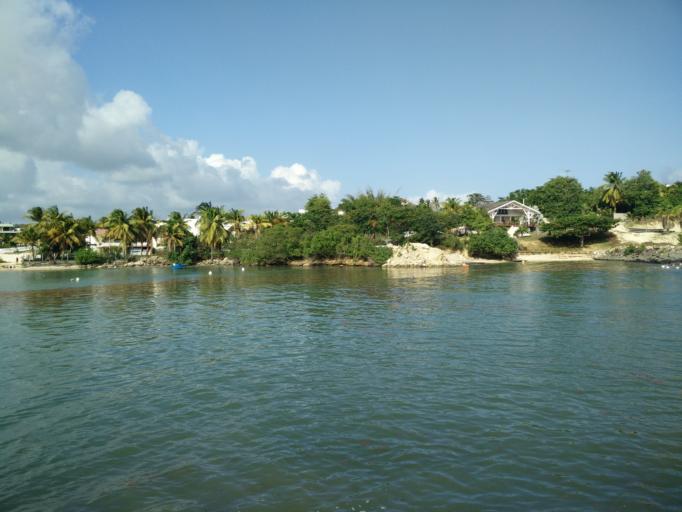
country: GP
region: Guadeloupe
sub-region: Guadeloupe
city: Le Gosier
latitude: 16.2011
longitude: -61.4566
